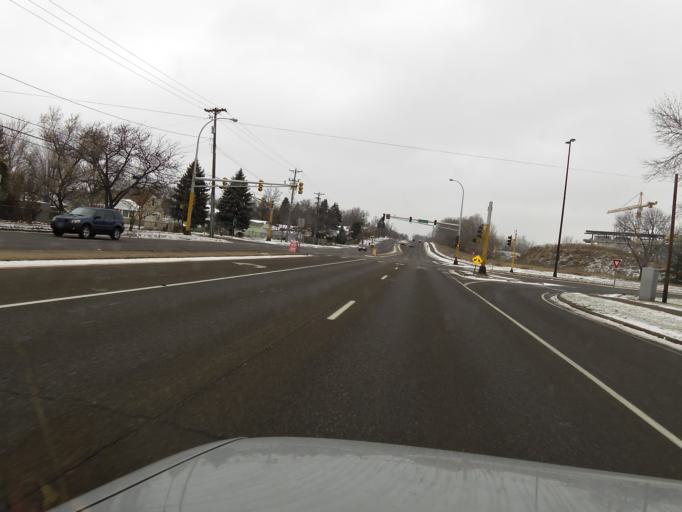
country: US
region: Minnesota
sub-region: Ramsey County
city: Maplewood
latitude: 44.9553
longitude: -93.0049
